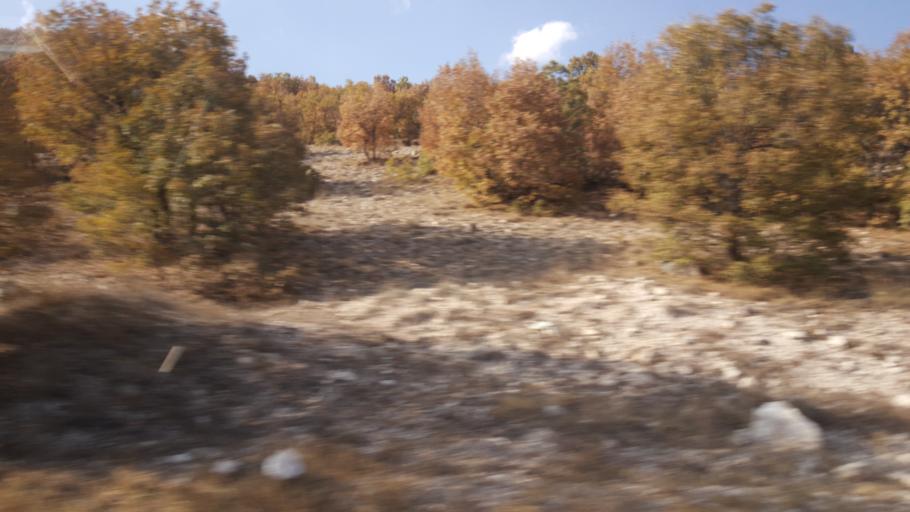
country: TR
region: Eskisehir
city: Kirka
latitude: 39.3460
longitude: 30.5859
